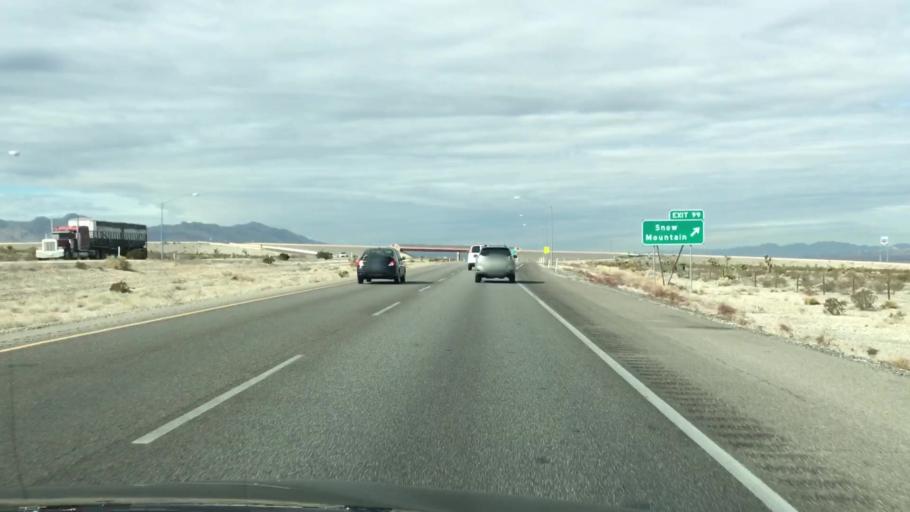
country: US
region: Nevada
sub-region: Clark County
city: Summerlin South
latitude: 36.3583
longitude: -115.3463
